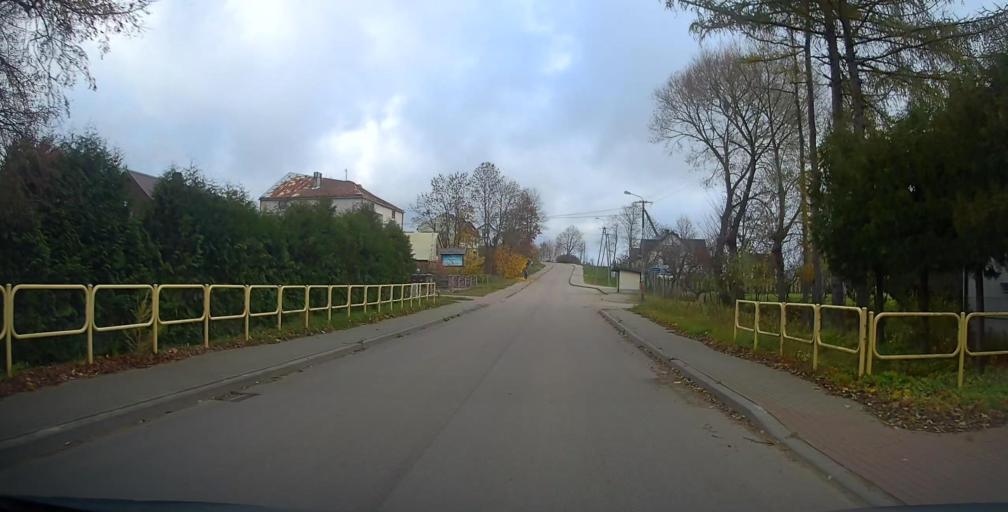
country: PL
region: Podlasie
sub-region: Suwalki
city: Suwalki
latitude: 54.2882
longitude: 22.8808
